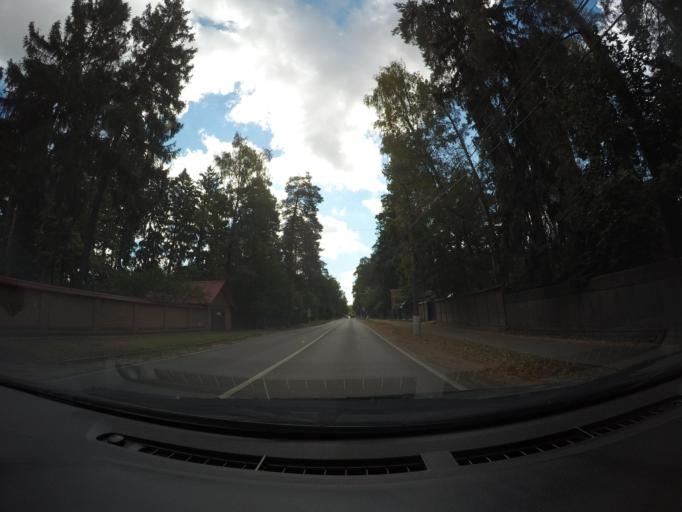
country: RU
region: Moskovskaya
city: Il'inskiy
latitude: 55.6247
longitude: 38.1126
